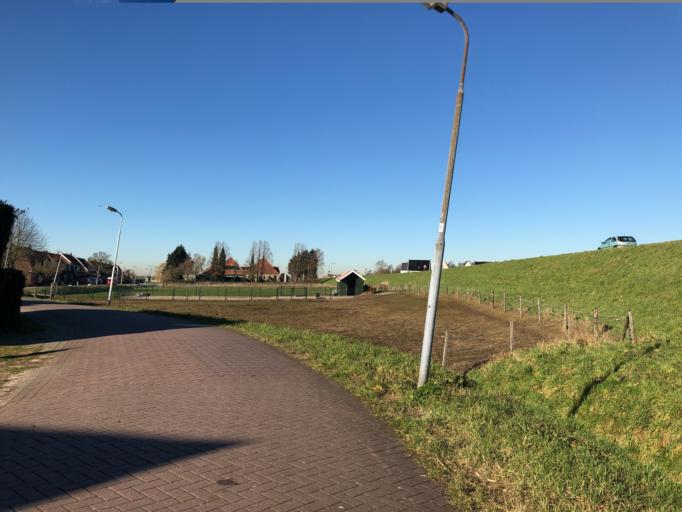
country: NL
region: North Holland
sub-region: Gemeente Zaanstad
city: Zaanstad
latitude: 52.4329
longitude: 4.7791
